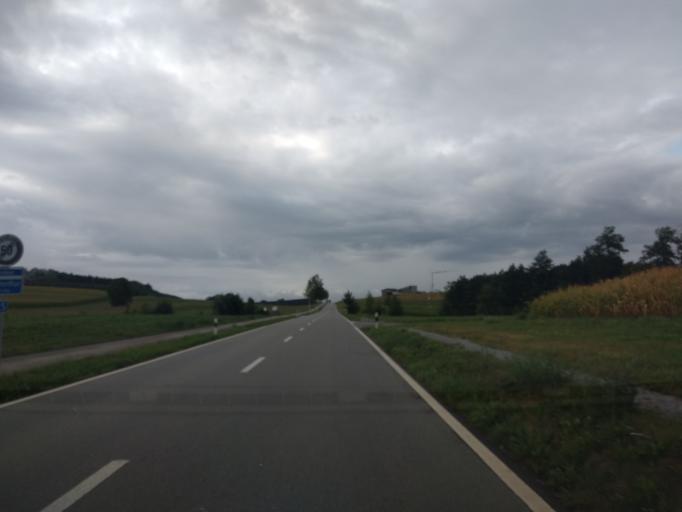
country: CH
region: Zurich
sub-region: Bezirk Andelfingen
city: Uhwiesen
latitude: 47.6667
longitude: 8.6392
